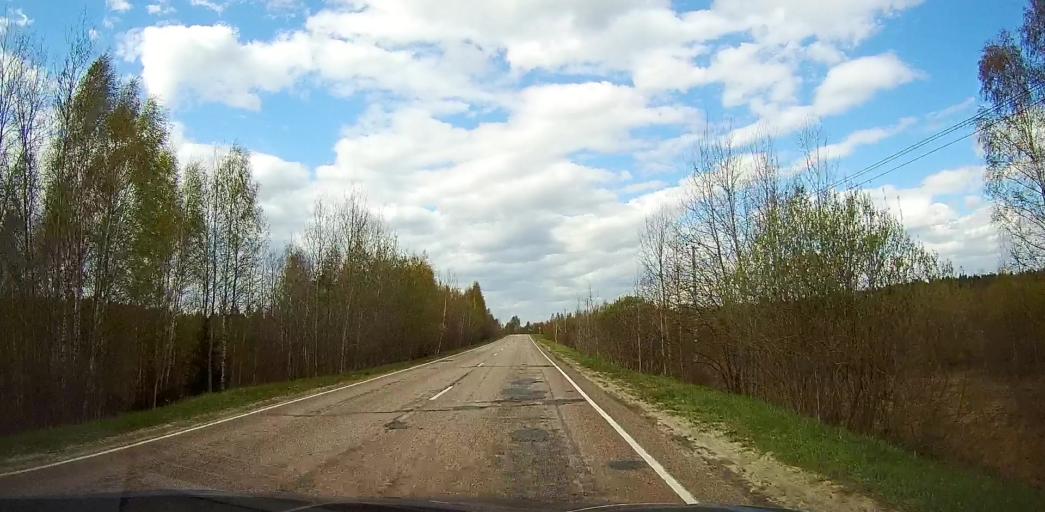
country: RU
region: Moskovskaya
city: Rakhmanovo
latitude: 55.6744
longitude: 38.6454
